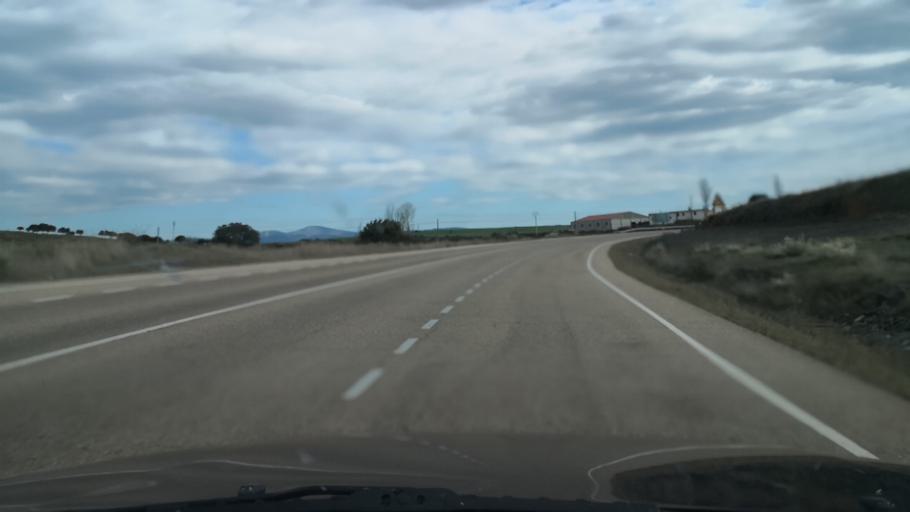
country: ES
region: Castille and Leon
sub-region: Provincia de Salamanca
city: Herguijuela de Ciudad Rodrigo
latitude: 40.4810
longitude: -6.5780
